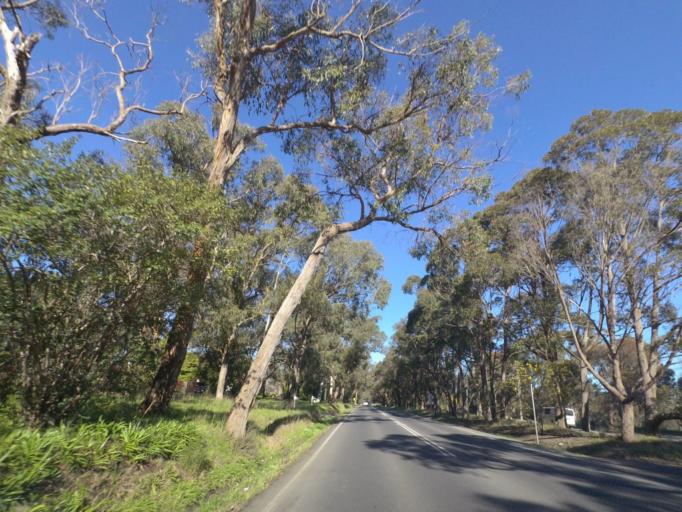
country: AU
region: Victoria
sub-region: Yarra Ranges
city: Kilsyth
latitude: -37.7964
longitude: 145.3246
